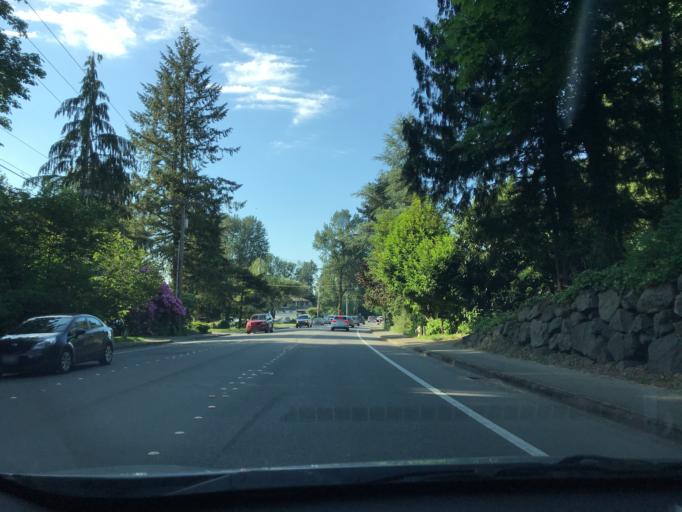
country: US
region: Washington
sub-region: King County
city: Issaquah
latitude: 47.5245
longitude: -122.0361
